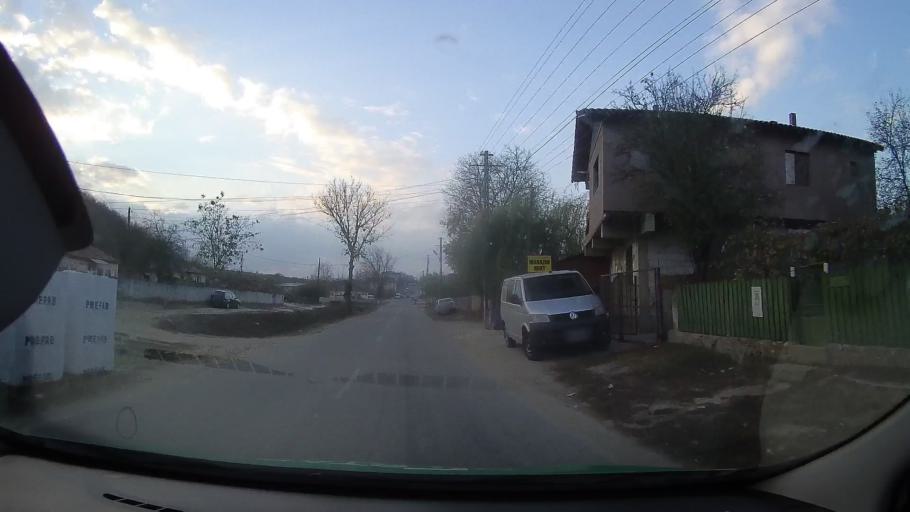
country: RO
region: Constanta
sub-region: Comuna Baneasa
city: Baneasa
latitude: 44.0623
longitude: 27.7044
